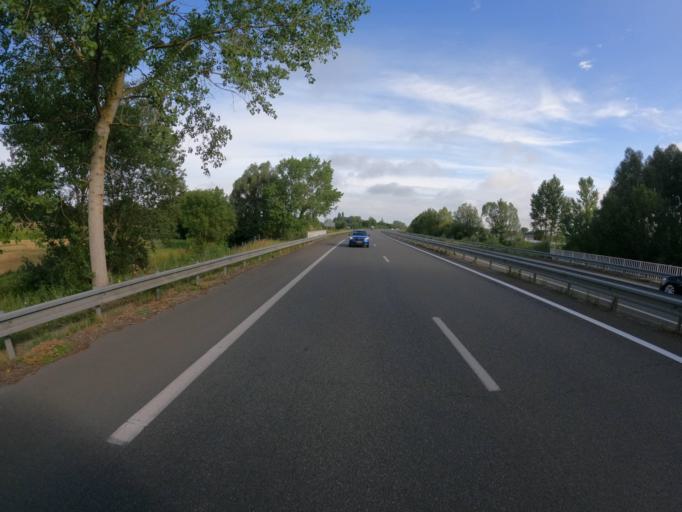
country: FR
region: Pays de la Loire
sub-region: Departement de Maine-et-Loire
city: Vivy
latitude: 47.3006
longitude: -0.0310
